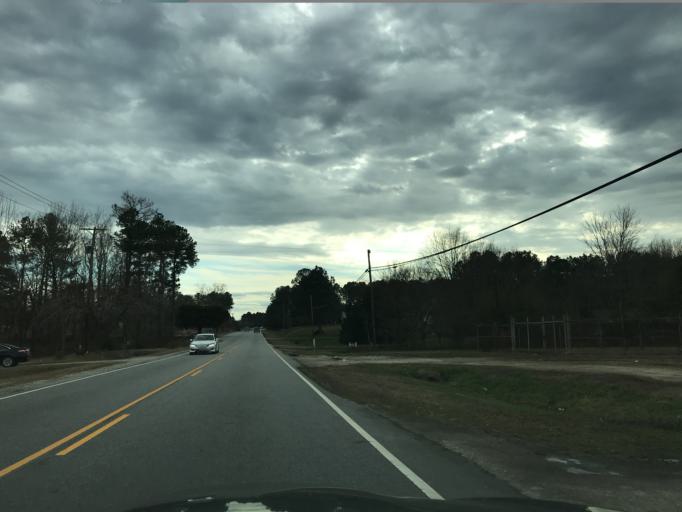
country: US
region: North Carolina
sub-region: Franklin County
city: Louisburg
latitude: 36.1246
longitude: -78.2950
